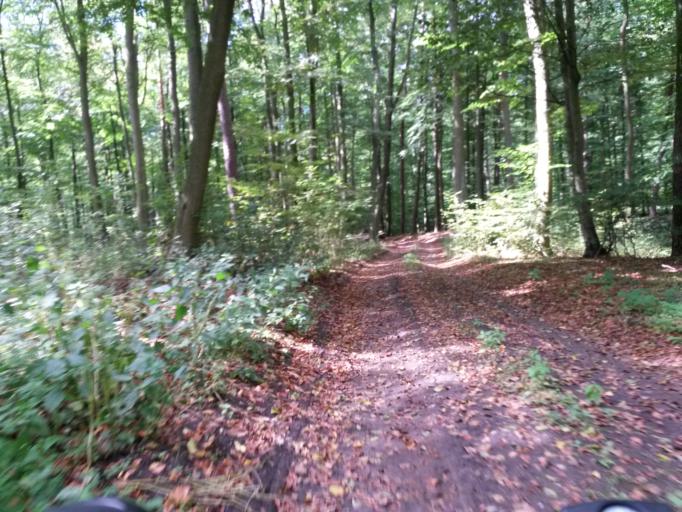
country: DE
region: Brandenburg
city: Milmersdorf
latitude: 53.1405
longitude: 13.5926
